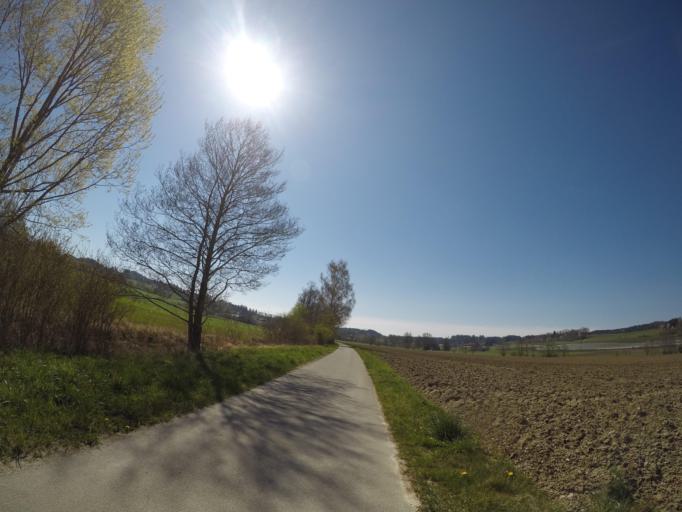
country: DE
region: Baden-Wuerttemberg
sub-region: Tuebingen Region
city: Horgenzell
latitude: 47.8300
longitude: 9.4562
